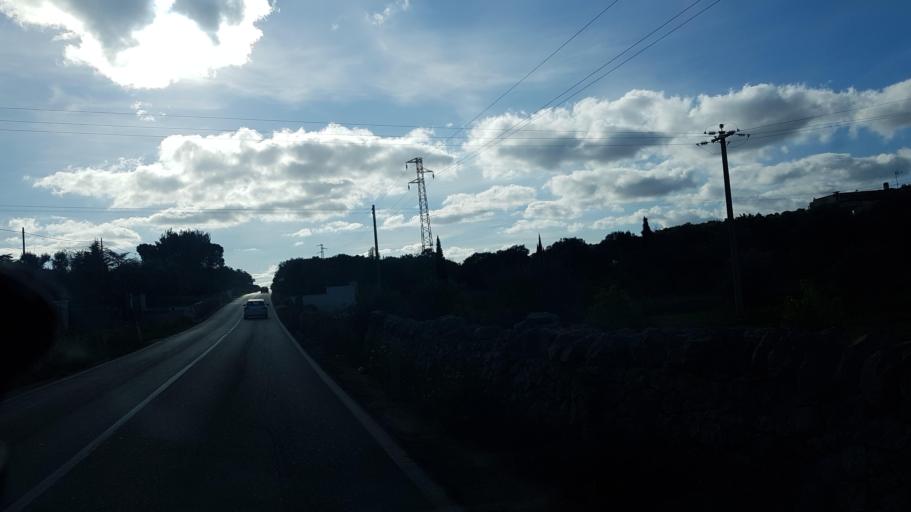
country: IT
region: Apulia
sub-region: Provincia di Brindisi
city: Ostuni
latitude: 40.6945
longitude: 17.5566
